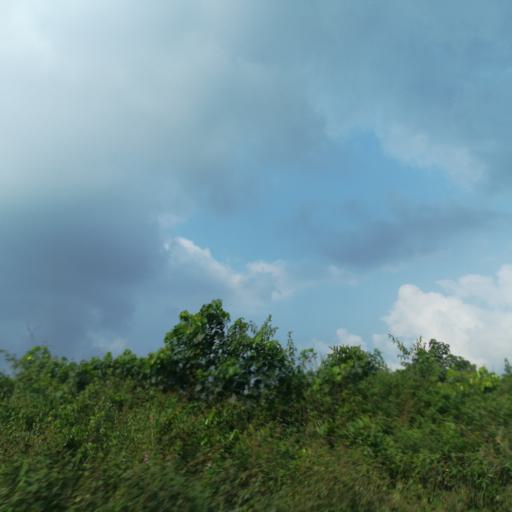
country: NG
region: Rivers
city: Okrika
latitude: 4.8174
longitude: 7.1251
